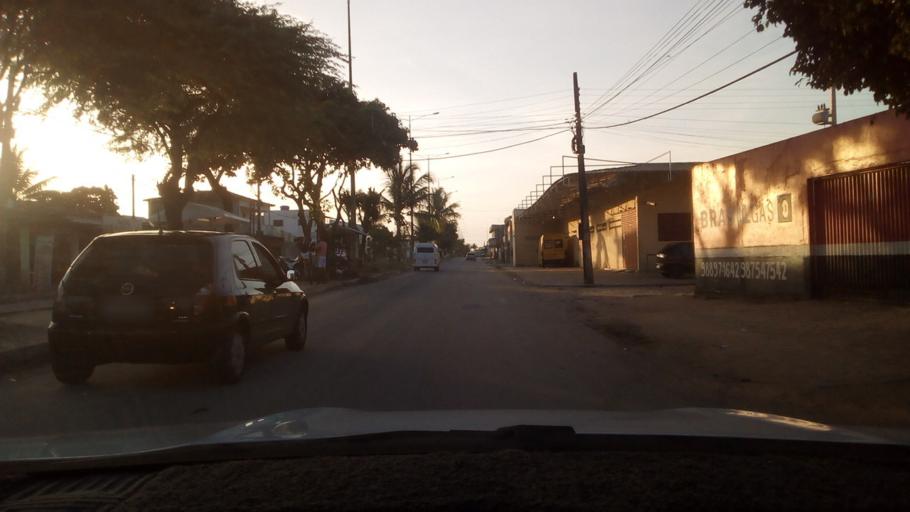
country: BR
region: Paraiba
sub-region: Bayeux
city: Bayeux
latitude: -7.1764
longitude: -34.9255
